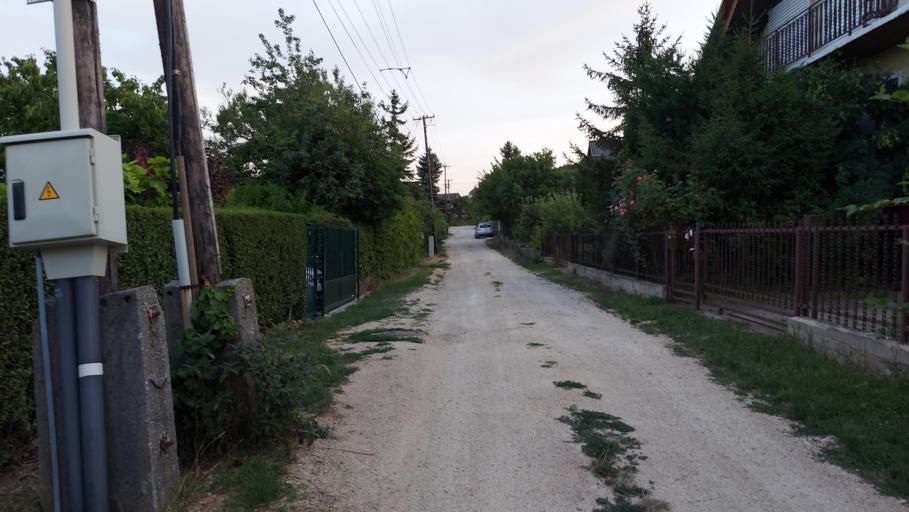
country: HU
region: Veszprem
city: Balatonalmadi
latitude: 47.0489
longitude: 18.0031
